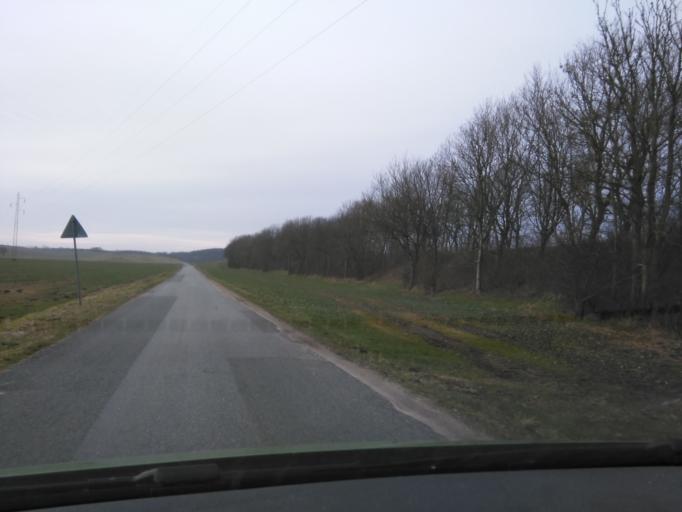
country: DK
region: Central Jutland
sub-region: Odder Kommune
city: Odder
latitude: 55.9244
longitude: 10.1063
